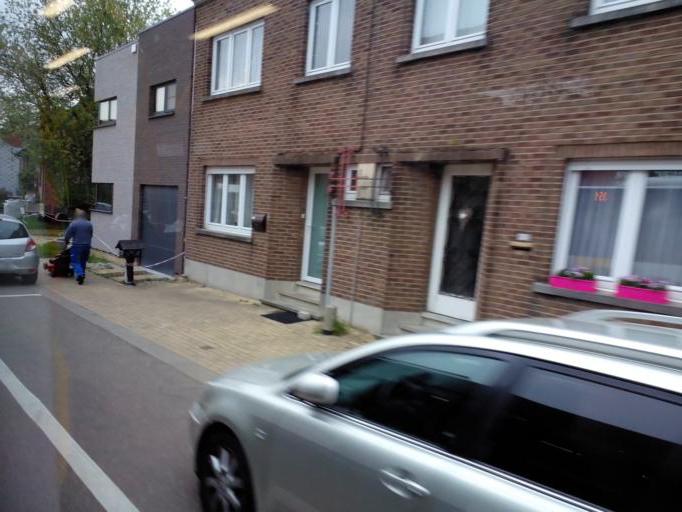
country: BE
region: Flanders
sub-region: Provincie Vlaams-Brabant
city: Kortenberg
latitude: 50.8769
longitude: 4.5408
